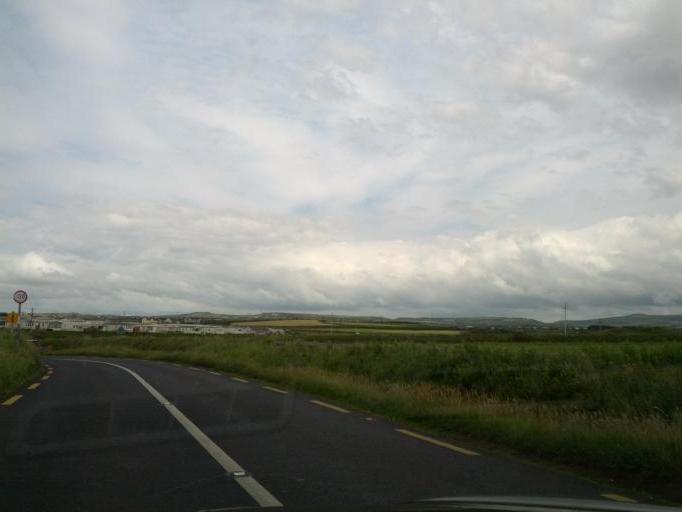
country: IE
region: Munster
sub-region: An Clar
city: Kilrush
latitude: 52.8358
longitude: -9.4300
